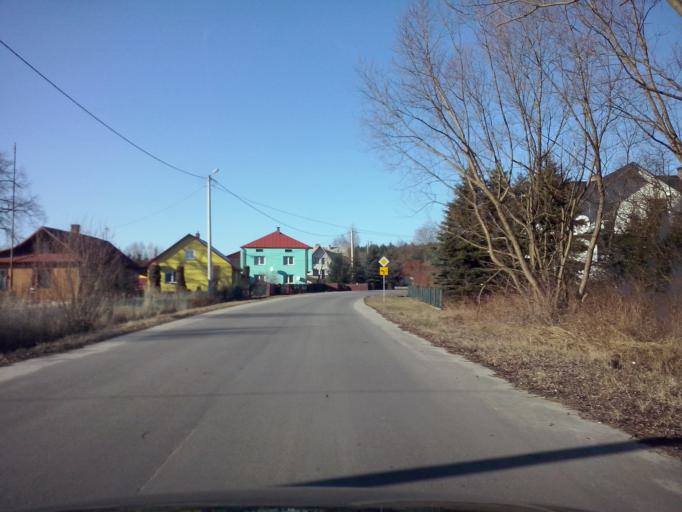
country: PL
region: Subcarpathian Voivodeship
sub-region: Powiat nizanski
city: Harasiuki
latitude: 50.5274
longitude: 22.4498
